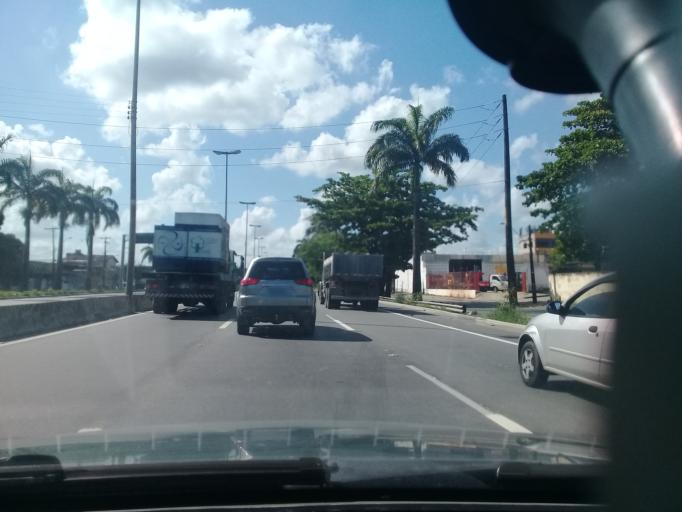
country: BR
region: Pernambuco
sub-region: Recife
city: Recife
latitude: -8.0328
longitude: -34.9421
